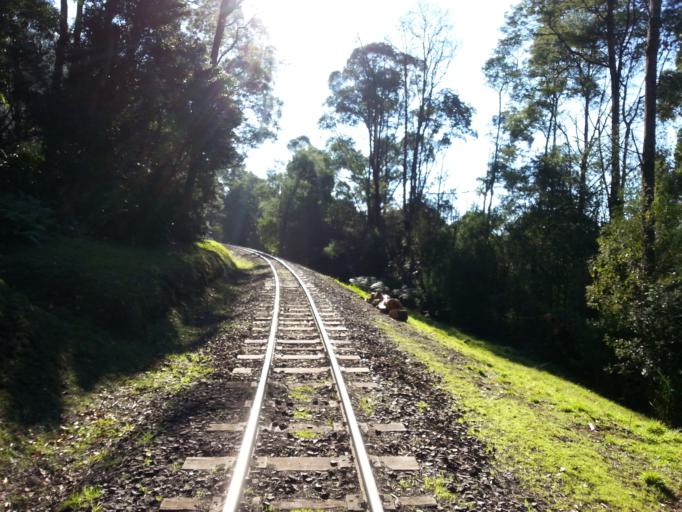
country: AU
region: Victoria
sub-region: Cardinia
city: Emerald
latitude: -37.9331
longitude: 145.4588
